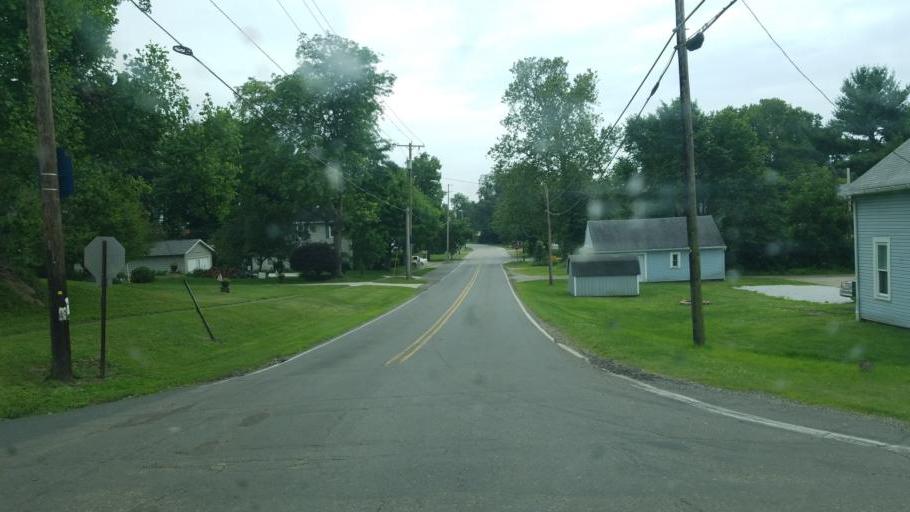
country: US
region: Ohio
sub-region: Summit County
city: Clinton
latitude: 40.9276
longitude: -81.6270
